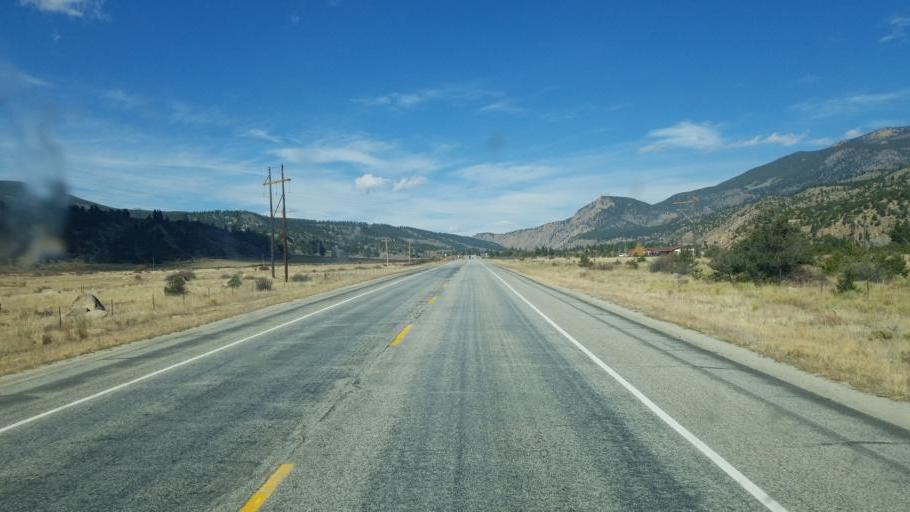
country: US
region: Colorado
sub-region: Chaffee County
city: Buena Vista
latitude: 38.9501
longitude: -106.1960
